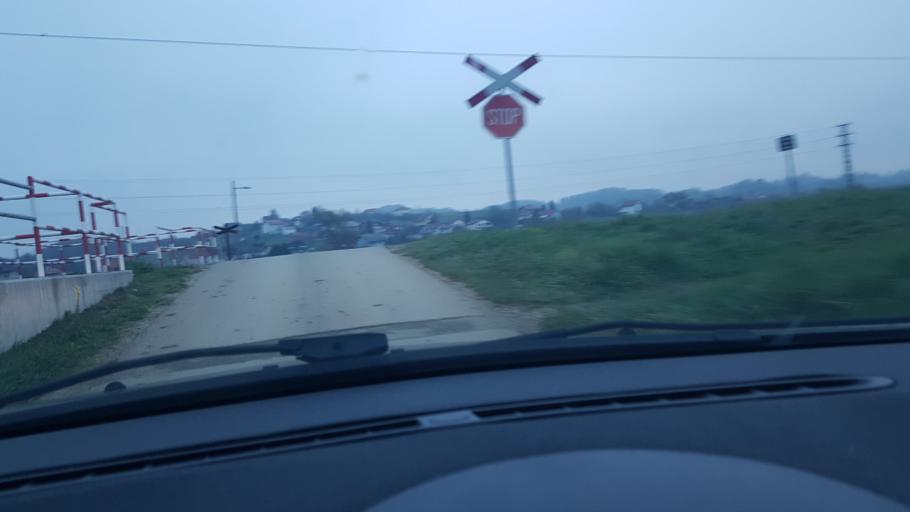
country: HR
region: Krapinsko-Zagorska
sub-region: Grad Krapina
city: Krapina
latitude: 46.1367
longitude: 15.8776
